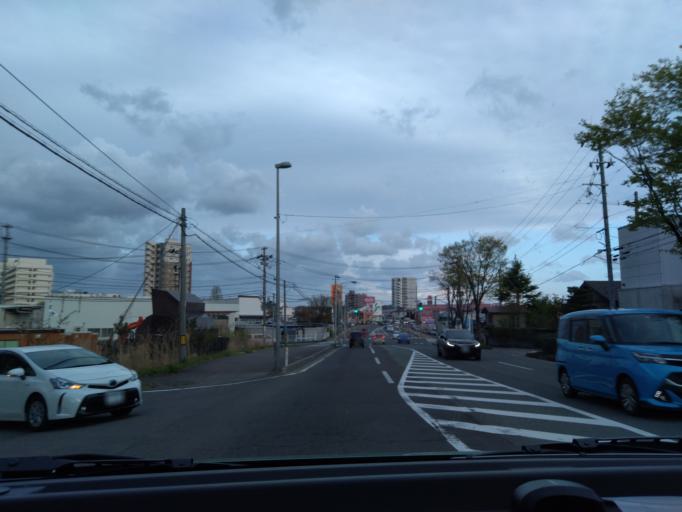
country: JP
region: Akita
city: Akita
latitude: 39.7312
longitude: 140.1446
